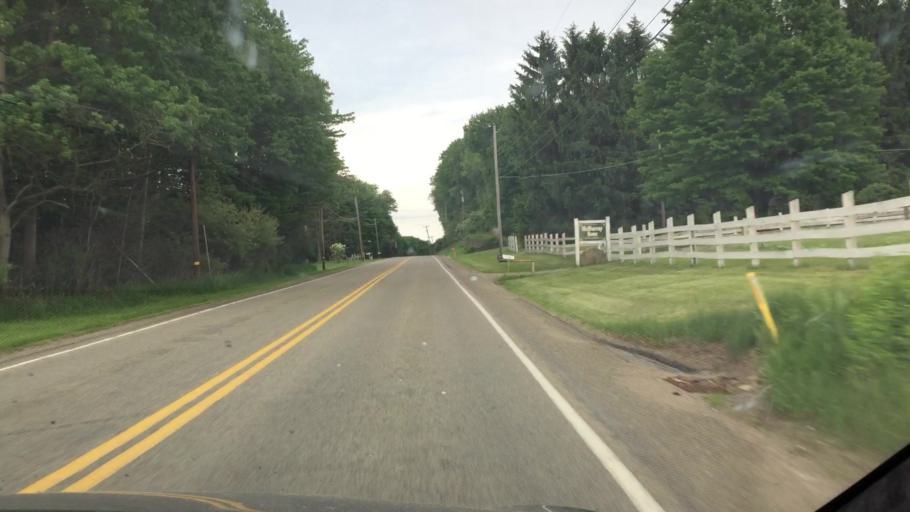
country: US
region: Pennsylvania
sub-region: Butler County
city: Slippery Rock
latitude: 41.0220
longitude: -80.0167
